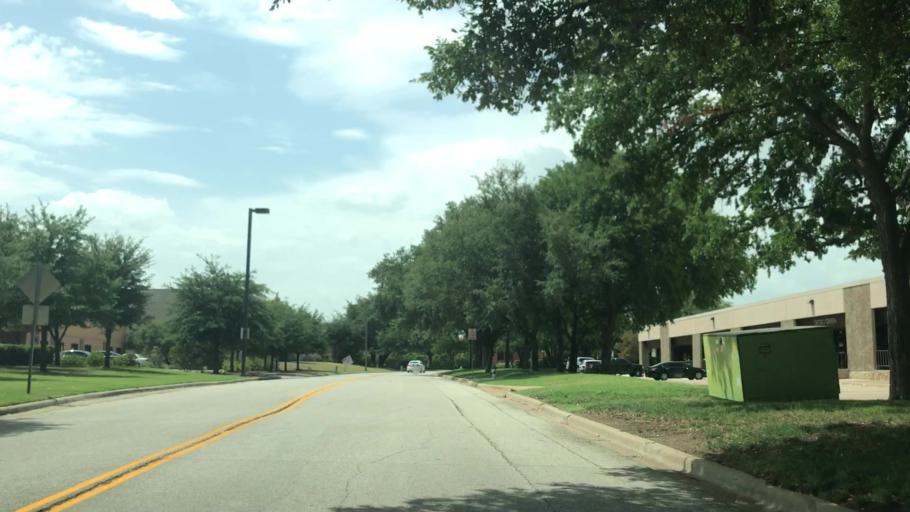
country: US
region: Texas
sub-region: Dallas County
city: Coppell
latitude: 32.8914
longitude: -96.9883
